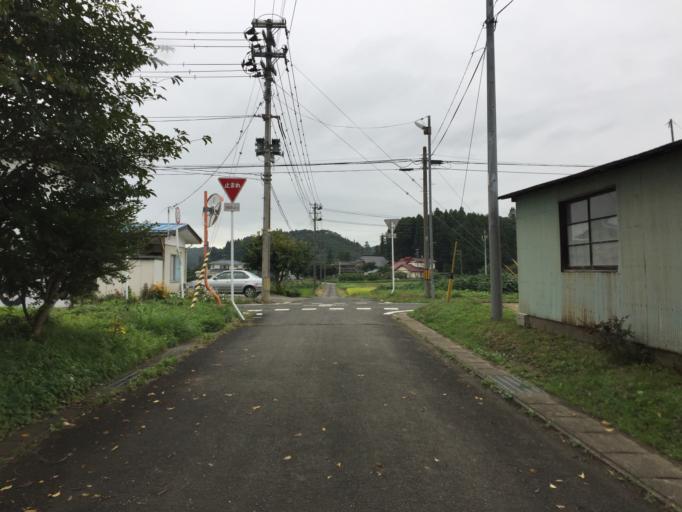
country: JP
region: Fukushima
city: Nihommatsu
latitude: 37.6542
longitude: 140.4470
